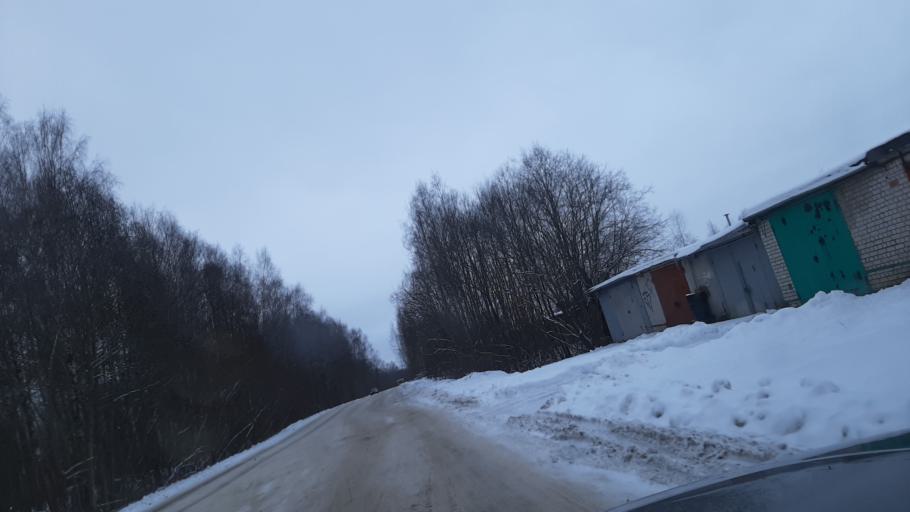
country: RU
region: Kostroma
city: Volgorechensk
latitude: 57.4448
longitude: 41.1337
